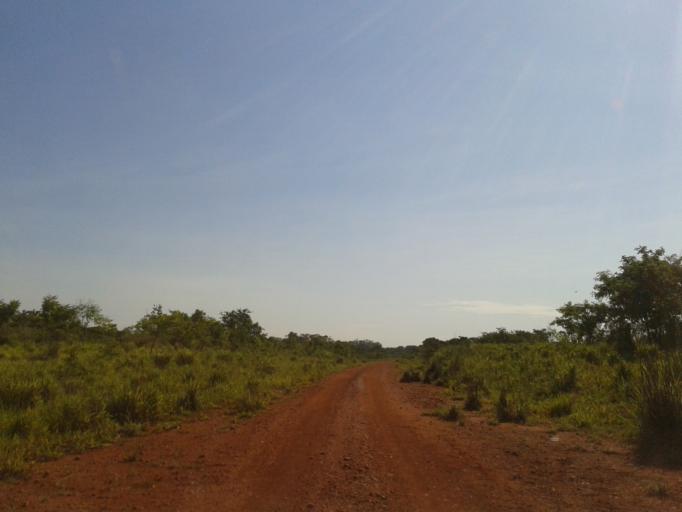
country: BR
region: Minas Gerais
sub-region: Santa Vitoria
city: Santa Vitoria
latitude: -19.1170
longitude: -50.5524
